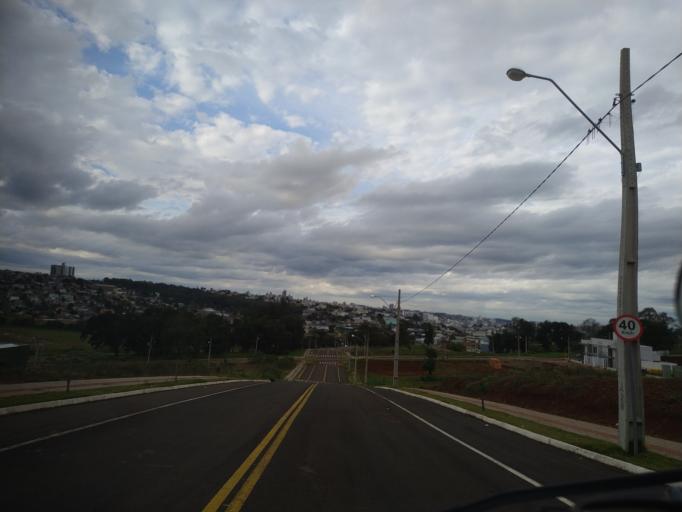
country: BR
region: Santa Catarina
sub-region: Chapeco
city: Chapeco
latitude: -27.0632
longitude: -52.6224
